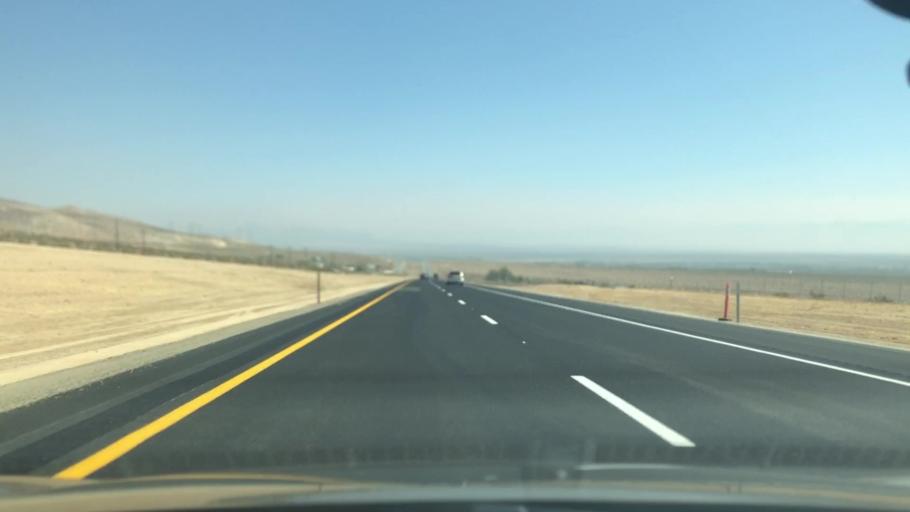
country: US
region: California
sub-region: Kern County
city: Inyokern
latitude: 35.6559
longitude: -117.8762
